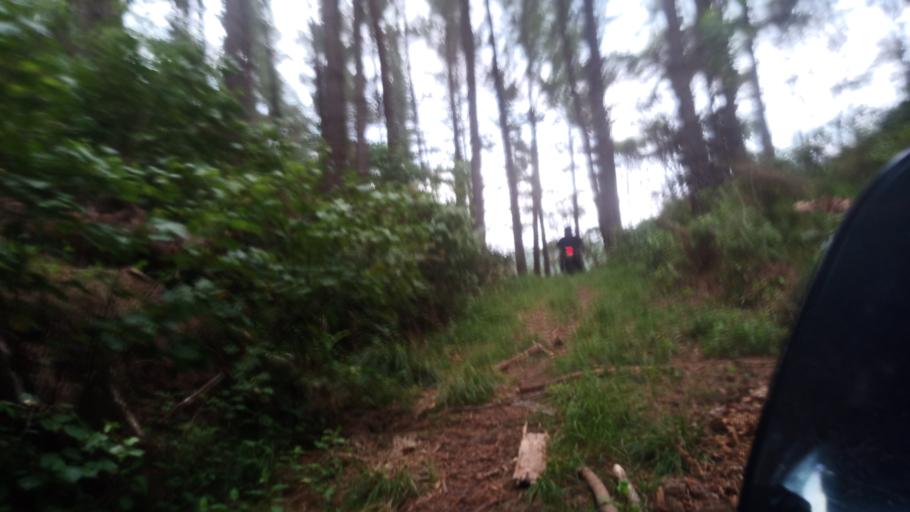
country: NZ
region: Gisborne
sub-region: Gisborne District
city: Gisborne
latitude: -38.4570
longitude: 177.9249
